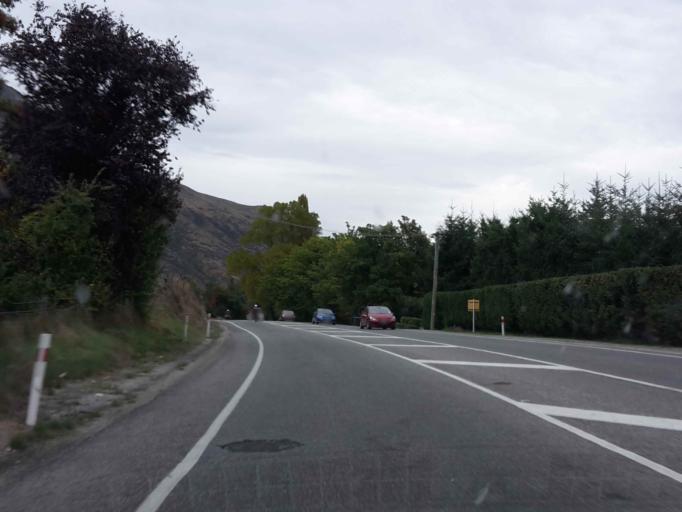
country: NZ
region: Otago
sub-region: Queenstown-Lakes District
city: Arrowtown
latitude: -44.9918
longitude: 168.8077
